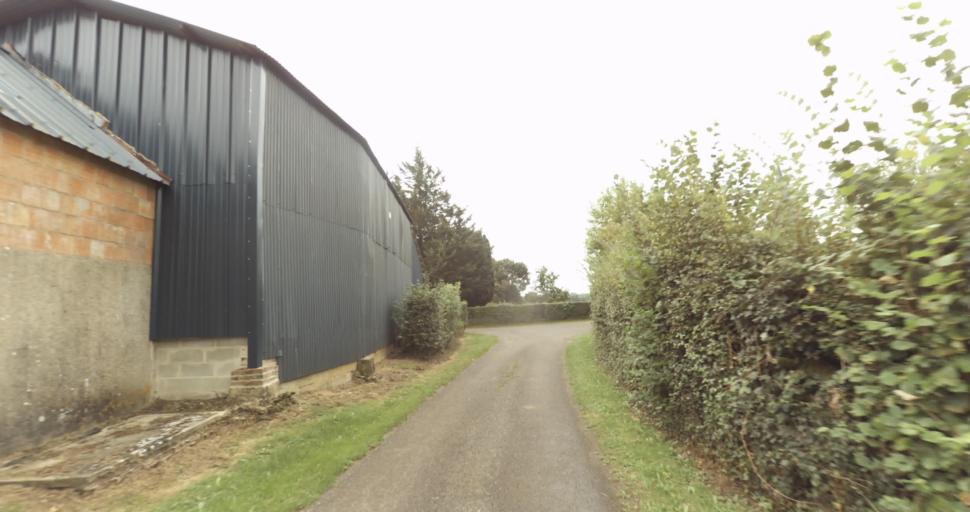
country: FR
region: Lower Normandy
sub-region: Departement de l'Orne
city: Gace
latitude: 48.7253
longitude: 0.3236
